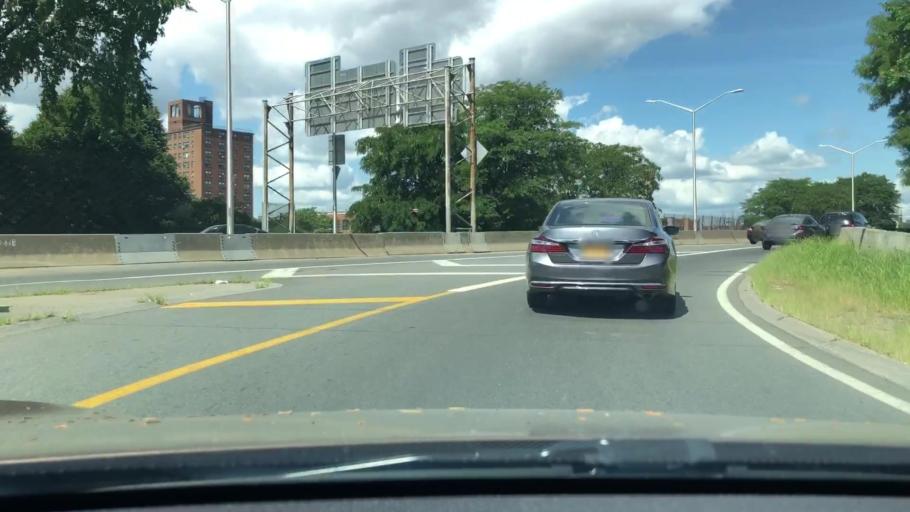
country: US
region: New York
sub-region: Bronx
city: The Bronx
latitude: 40.8236
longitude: -73.8721
